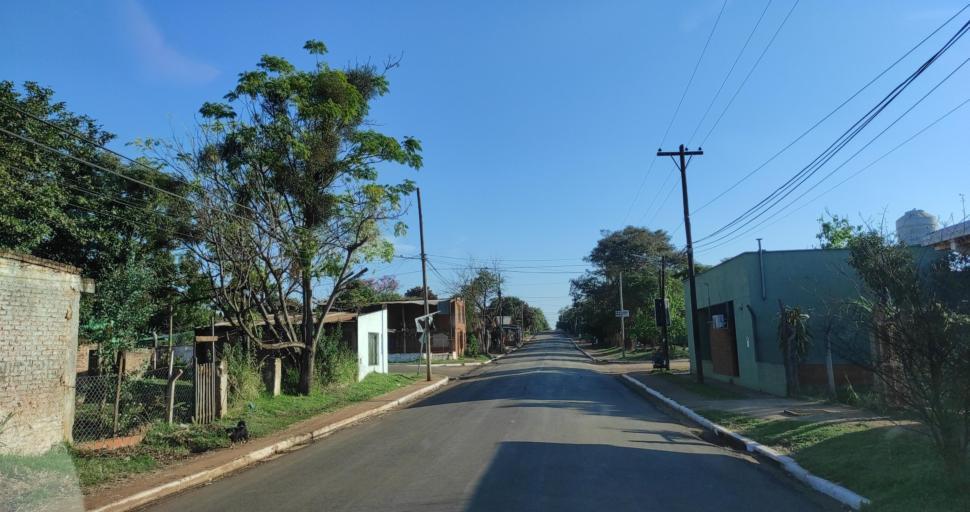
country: AR
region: Misiones
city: Garupa
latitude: -27.4473
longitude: -55.8596
